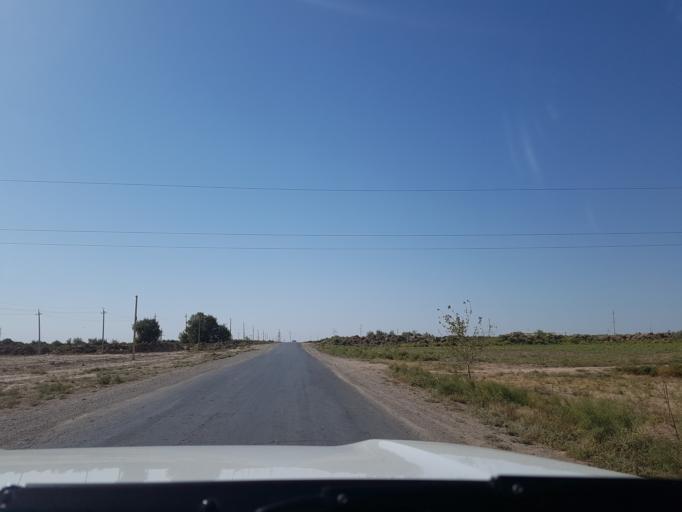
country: IR
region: Razavi Khorasan
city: Sarakhs
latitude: 36.5214
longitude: 61.2462
